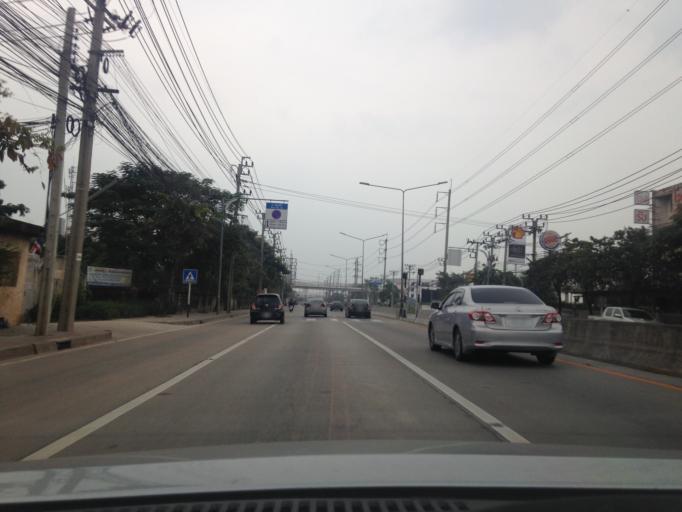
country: TH
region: Bangkok
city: Lat Krabang
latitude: 13.7404
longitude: 100.7465
